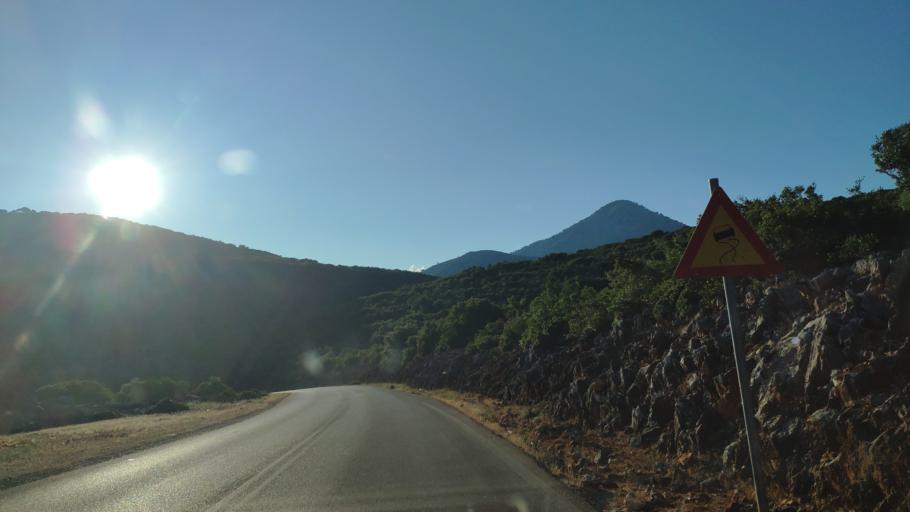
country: GR
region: West Greece
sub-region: Nomos Aitolias kai Akarnanias
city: Astakos
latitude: 38.6100
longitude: 21.1235
